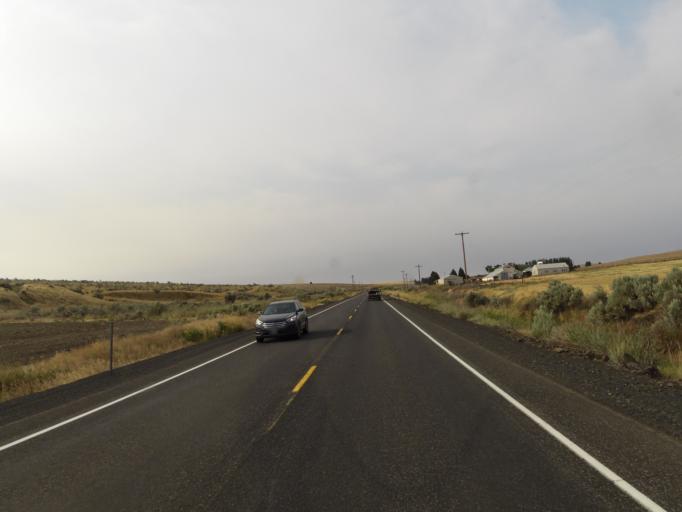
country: US
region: Oregon
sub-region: Sherman County
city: Moro
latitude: 45.4614
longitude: -120.7482
